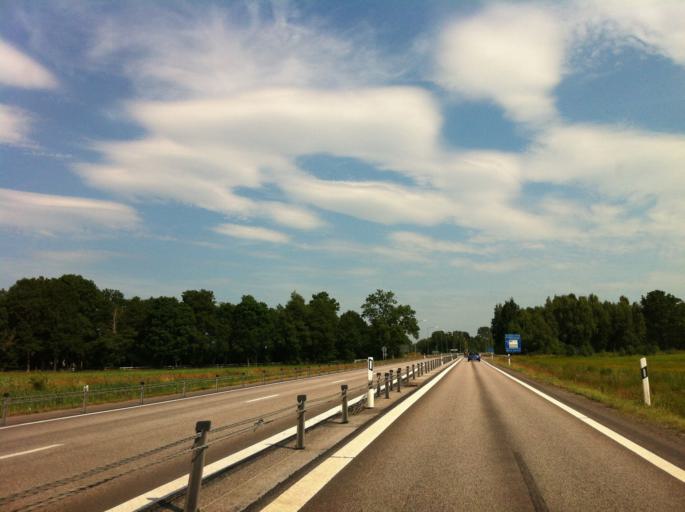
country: SE
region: Kalmar
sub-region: Kalmar Kommun
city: Trekanten
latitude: 56.7115
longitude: 16.0672
